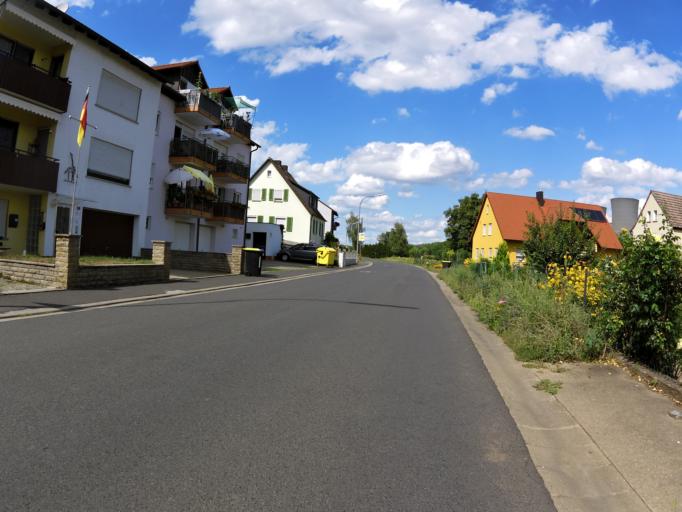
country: DE
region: Bavaria
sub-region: Regierungsbezirk Unterfranken
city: Bergrheinfeld
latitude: 49.9762
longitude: 10.1741
